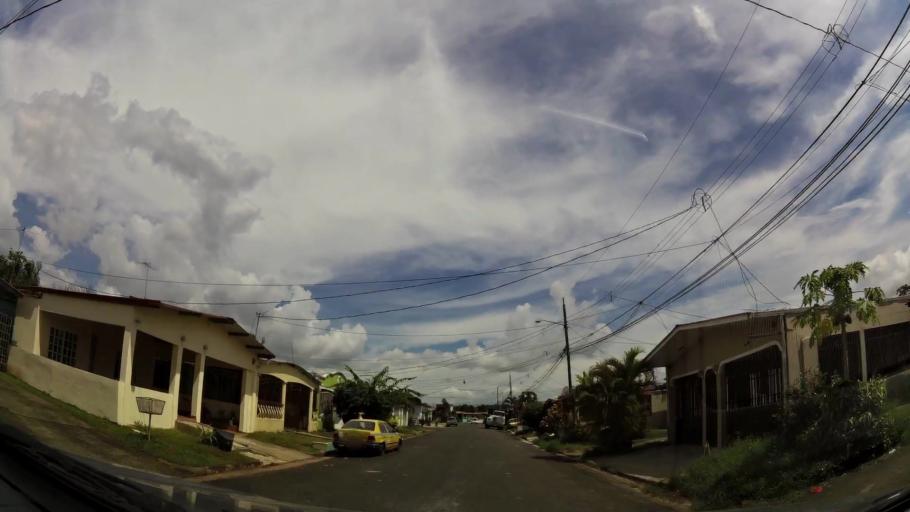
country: PA
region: Panama
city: Nuevo Arraijan
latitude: 8.9117
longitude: -79.7089
